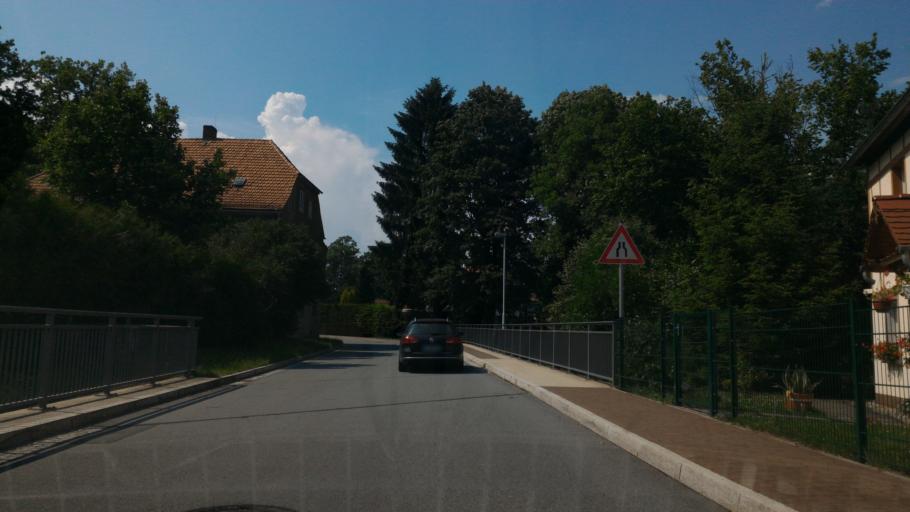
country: DE
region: Saxony
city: Hirschfelde
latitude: 50.9425
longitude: 14.8385
